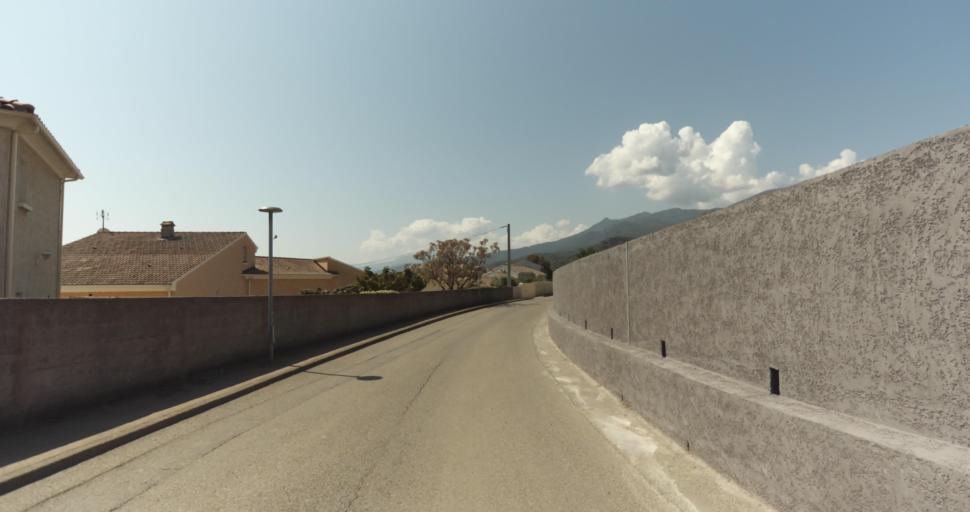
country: FR
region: Corsica
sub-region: Departement de la Haute-Corse
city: Biguglia
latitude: 42.6182
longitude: 9.4341
